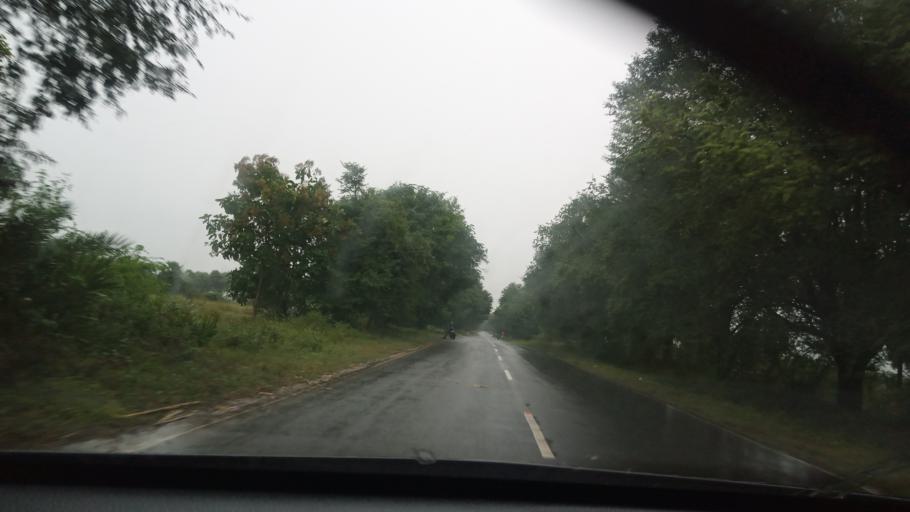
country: IN
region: Tamil Nadu
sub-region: Vellore
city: Kalavai
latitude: 12.8325
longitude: 79.4055
